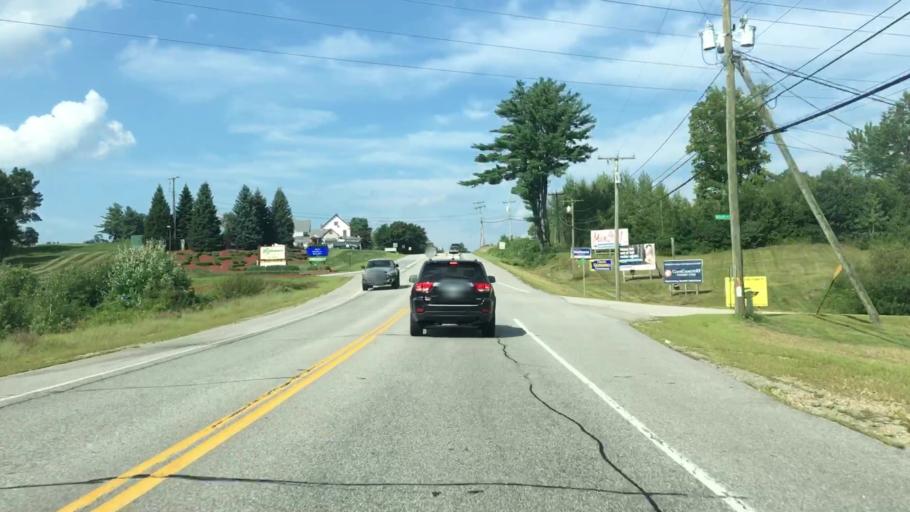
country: US
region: New Hampshire
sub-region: Belknap County
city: Sanbornton
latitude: 43.4658
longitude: -71.5480
